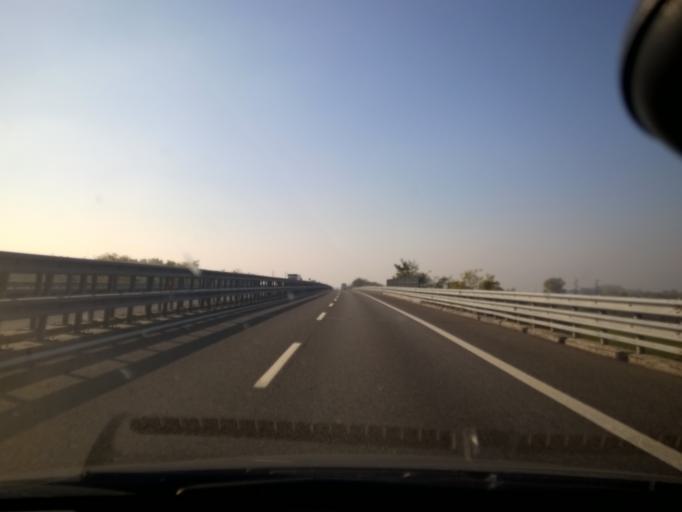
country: IT
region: Lombardy
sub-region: Provincia di Pavia
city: Pizzale
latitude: 45.0215
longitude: 9.0387
